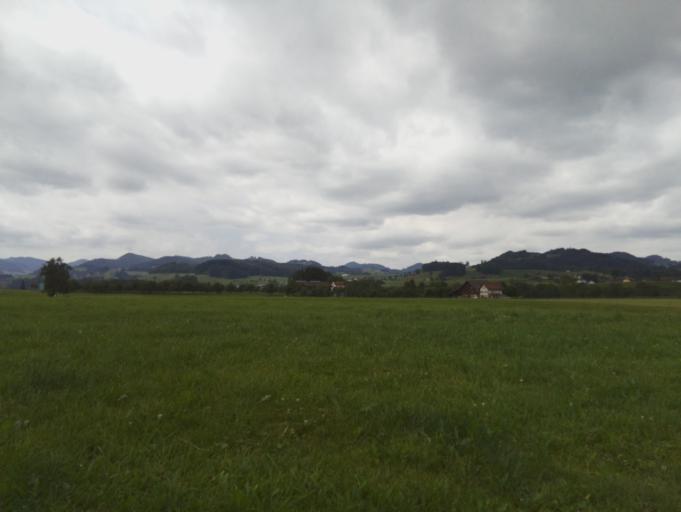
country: CH
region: Saint Gallen
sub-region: Wahlkreis Toggenburg
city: Lutisburg
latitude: 47.3897
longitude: 9.0866
